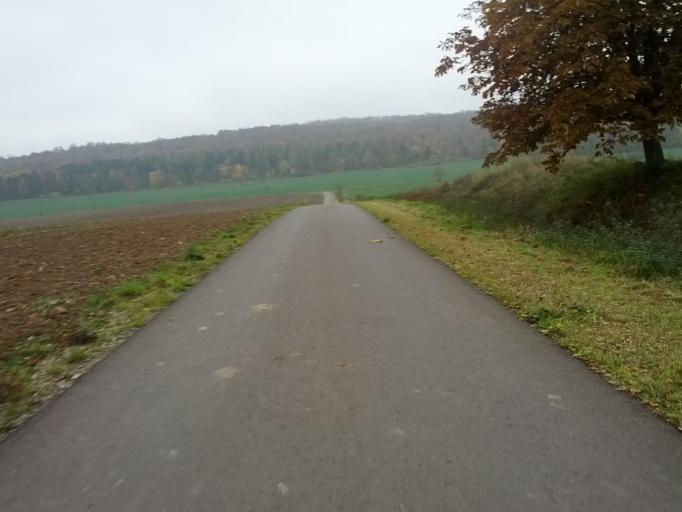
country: DE
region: Thuringia
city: Seebach
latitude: 50.9762
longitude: 10.4209
